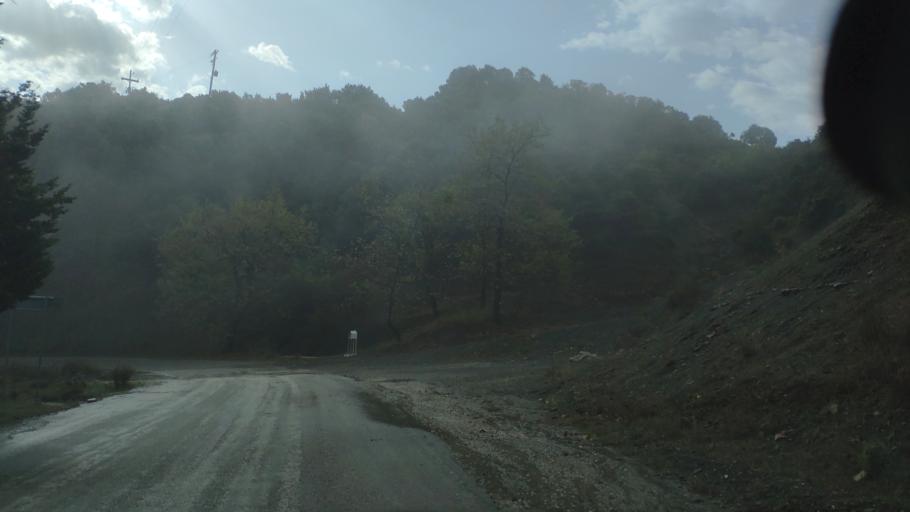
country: GR
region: West Greece
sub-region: Nomos Aitolias kai Akarnanias
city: Sardinia
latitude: 38.8701
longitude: 21.2824
